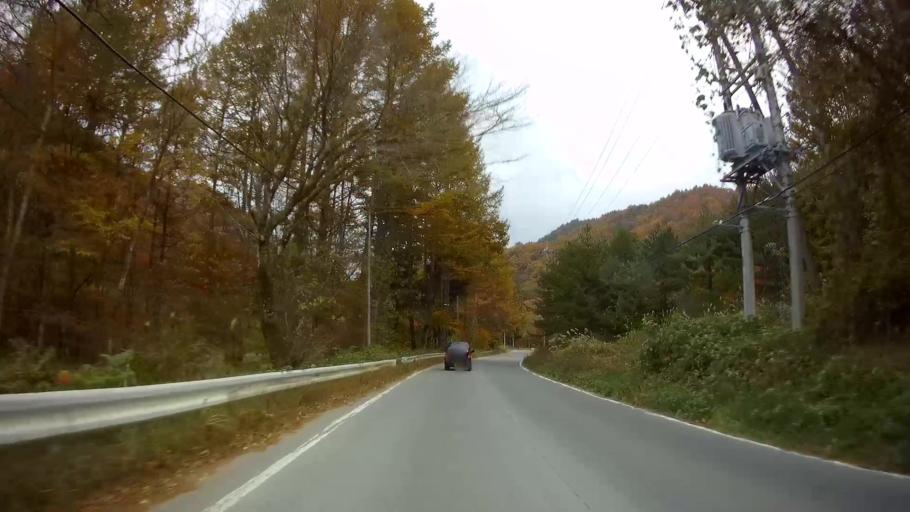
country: JP
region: Gunma
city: Nakanojomachi
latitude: 36.6276
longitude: 138.6497
